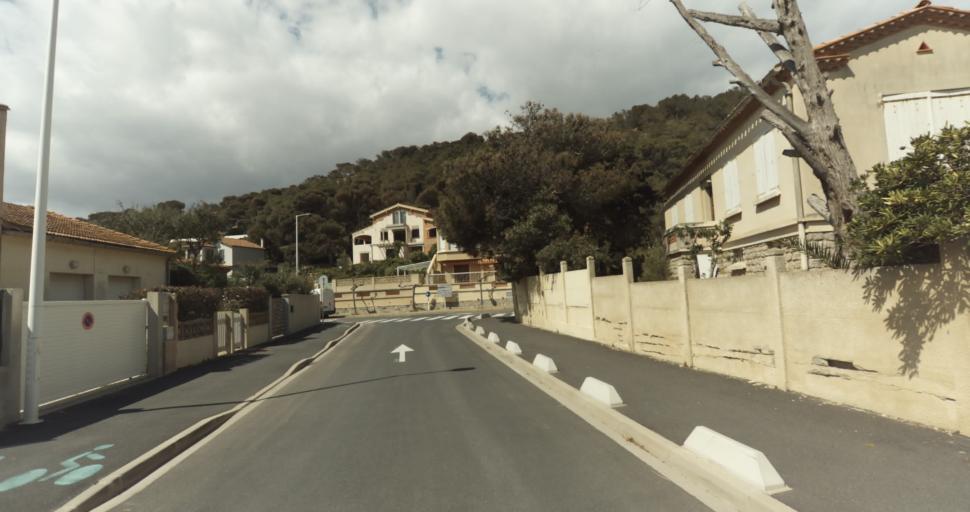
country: FR
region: Languedoc-Roussillon
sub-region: Departement de l'Aude
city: Leucate
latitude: 42.9060
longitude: 3.0556
